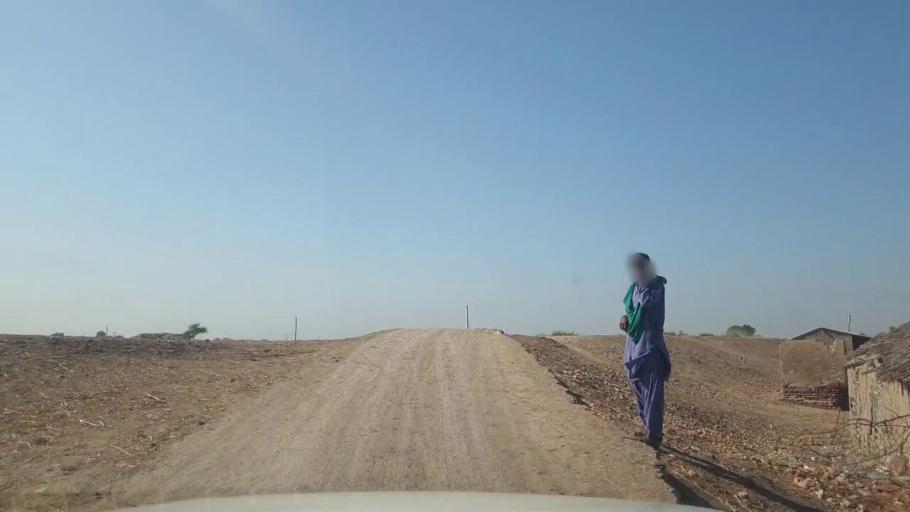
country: PK
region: Sindh
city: Chuhar Jamali
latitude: 24.4442
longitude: 67.8454
